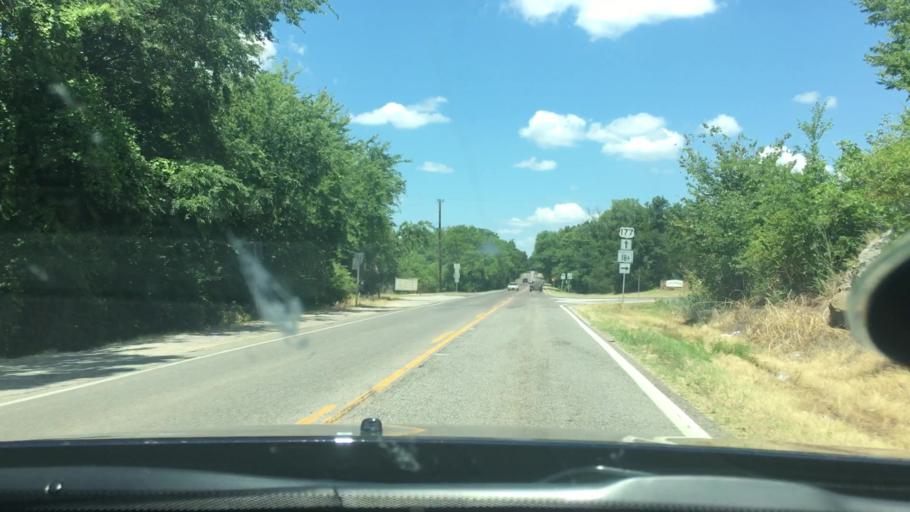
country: US
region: Oklahoma
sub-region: Murray County
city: Sulphur
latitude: 34.4909
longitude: -96.9660
